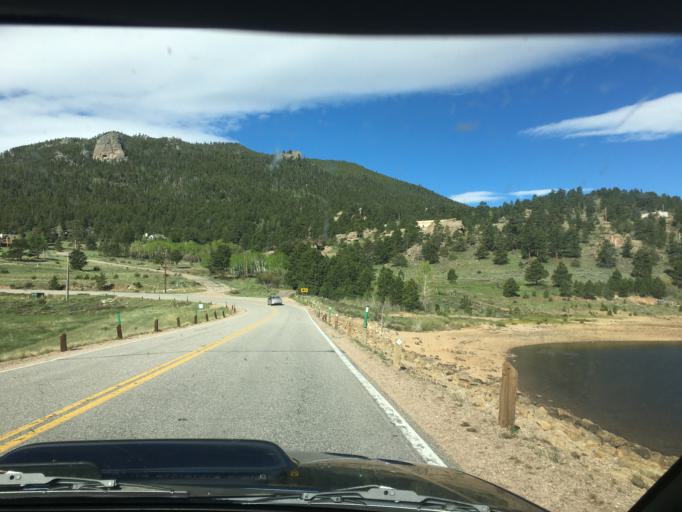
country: US
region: Colorado
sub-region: Larimer County
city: Estes Park
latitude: 40.3423
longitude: -105.5301
